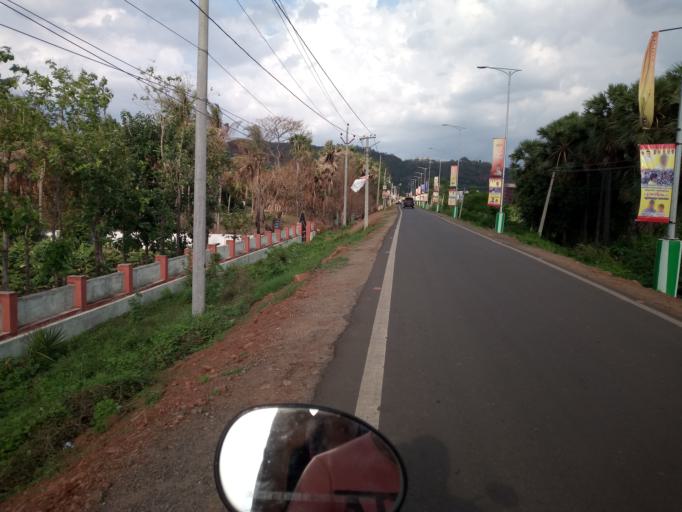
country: IN
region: Andhra Pradesh
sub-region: Guntur
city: Tadepalle
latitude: 16.5009
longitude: 80.5924
